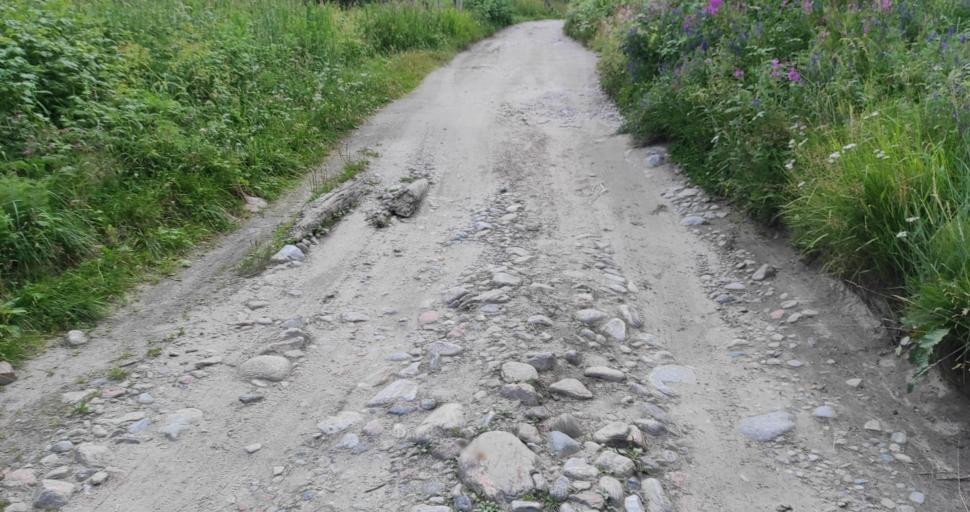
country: RU
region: Murmansk
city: Afrikanda
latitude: 67.0815
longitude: 32.9918
